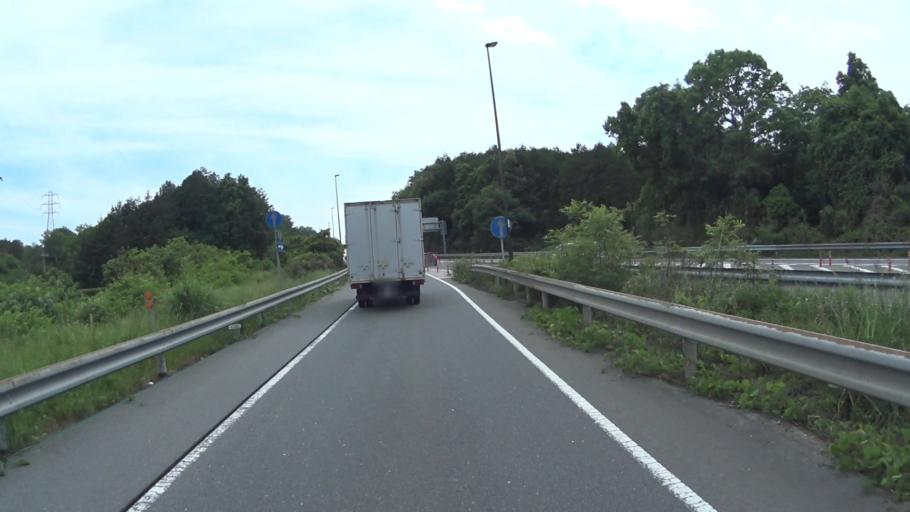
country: JP
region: Shiga Prefecture
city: Kitahama
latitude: 35.1311
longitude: 135.9029
